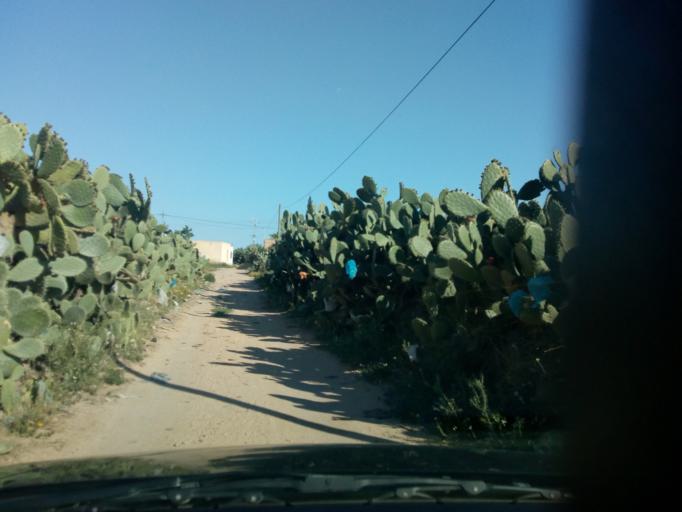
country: TN
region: Safaqis
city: Sfax
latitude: 34.7304
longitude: 10.6098
